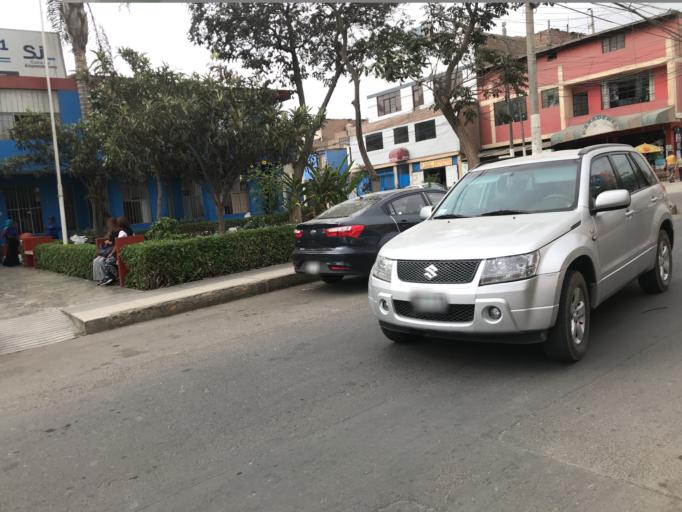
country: PE
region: Lima
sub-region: Lima
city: Independencia
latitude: -11.9728
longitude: -77.0048
